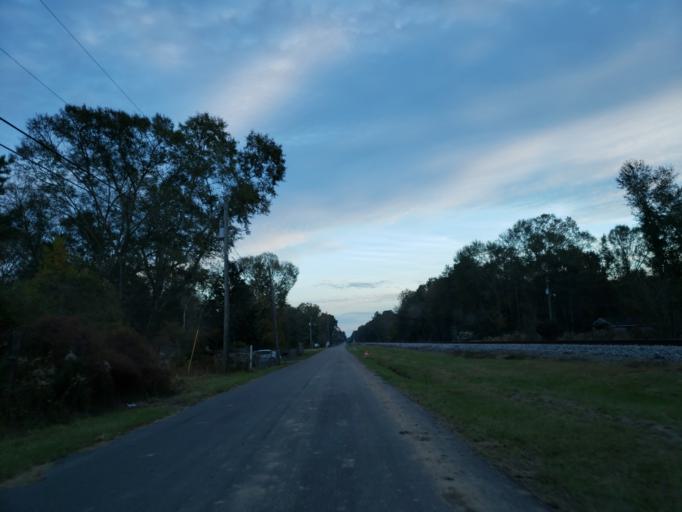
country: US
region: Mississippi
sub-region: Forrest County
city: Hattiesburg
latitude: 31.2803
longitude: -89.2571
